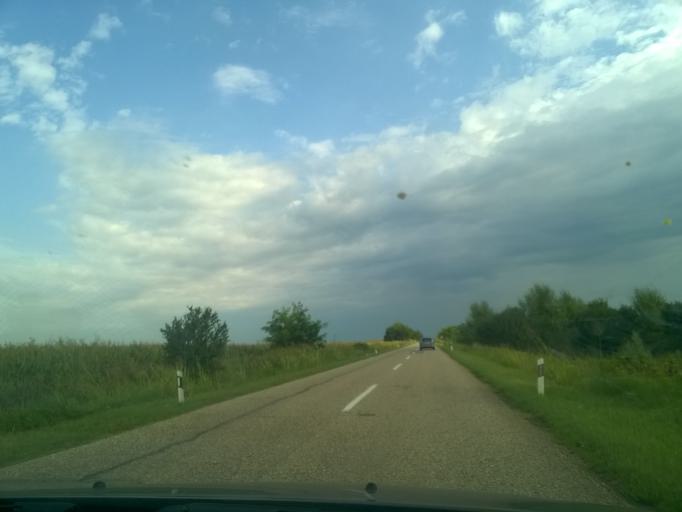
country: RS
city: Uzdin
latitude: 45.1689
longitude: 20.6175
